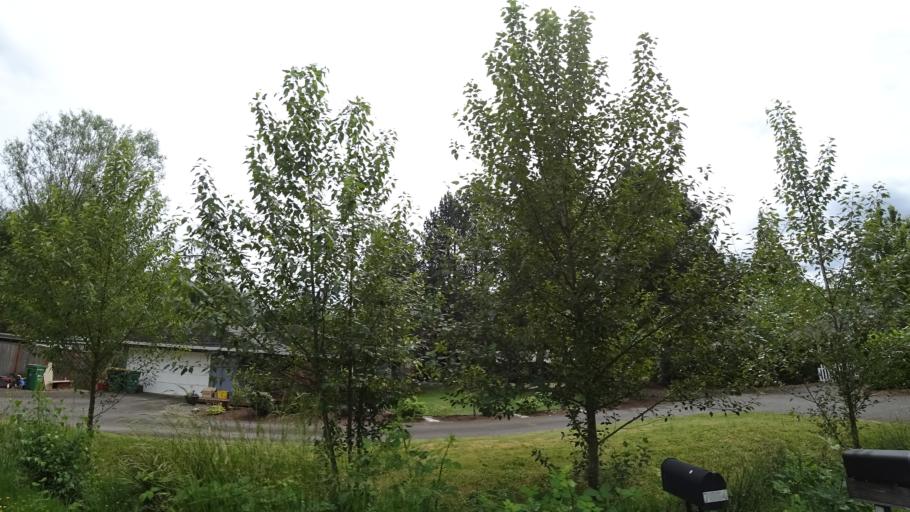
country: US
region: Oregon
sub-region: Washington County
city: Metzger
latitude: 45.4550
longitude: -122.7559
